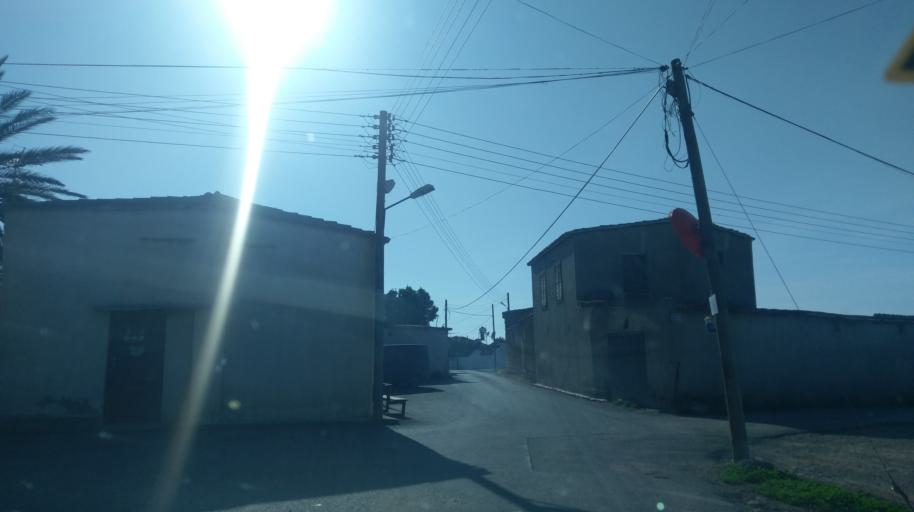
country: CY
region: Larnaka
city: Athienou
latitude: 35.1760
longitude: 33.5501
